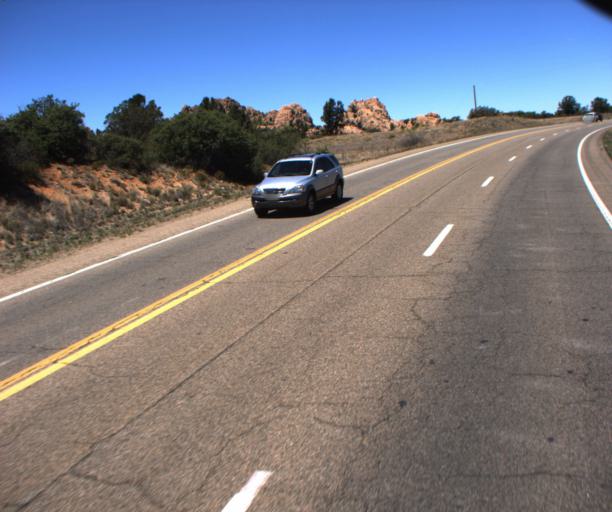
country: US
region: Arizona
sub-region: Yavapai County
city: Prescott
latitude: 34.6176
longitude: -112.4228
